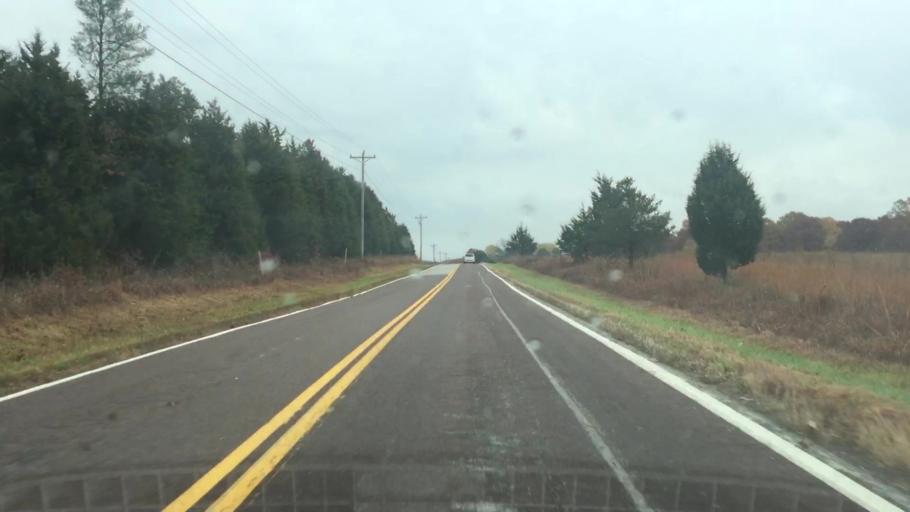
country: US
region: Missouri
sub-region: Callaway County
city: Fulton
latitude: 38.7827
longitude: -91.8247
